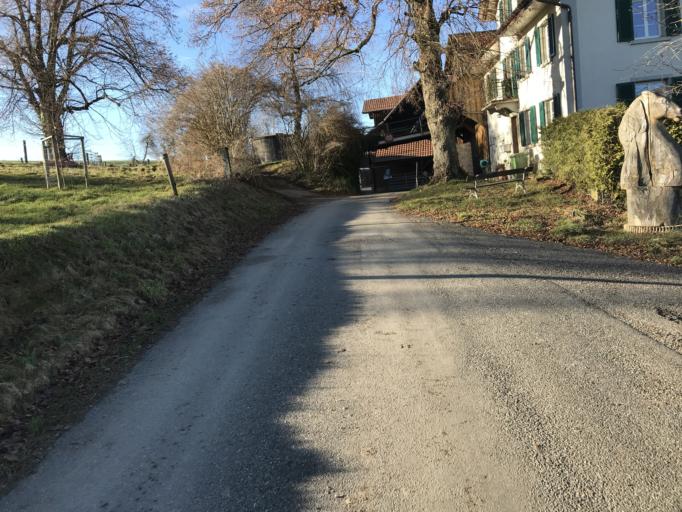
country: CH
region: Thurgau
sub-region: Frauenfeld District
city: Eschenz
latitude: 47.6323
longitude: 8.8574
